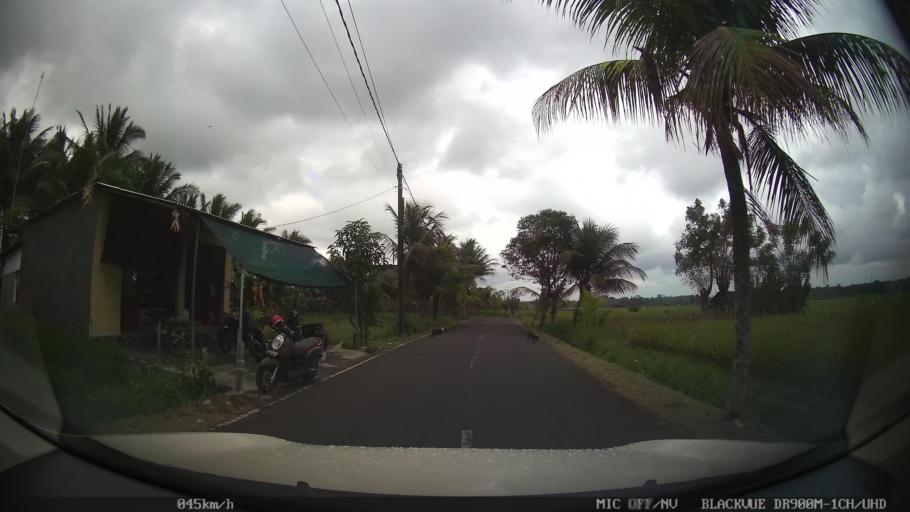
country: ID
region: Bali
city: Banjar Cemenggon
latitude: -8.5302
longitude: 115.1893
